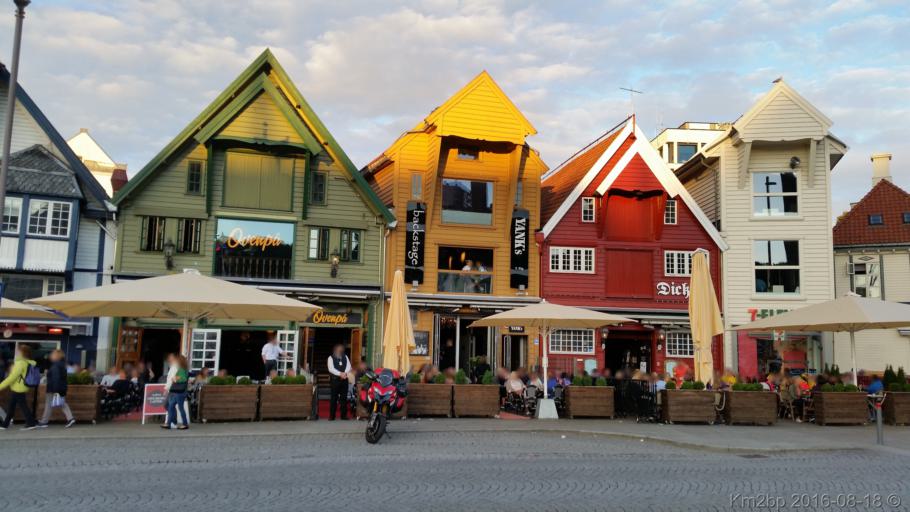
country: NO
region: Rogaland
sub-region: Stavanger
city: Stavanger
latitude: 58.9707
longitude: 5.7308
